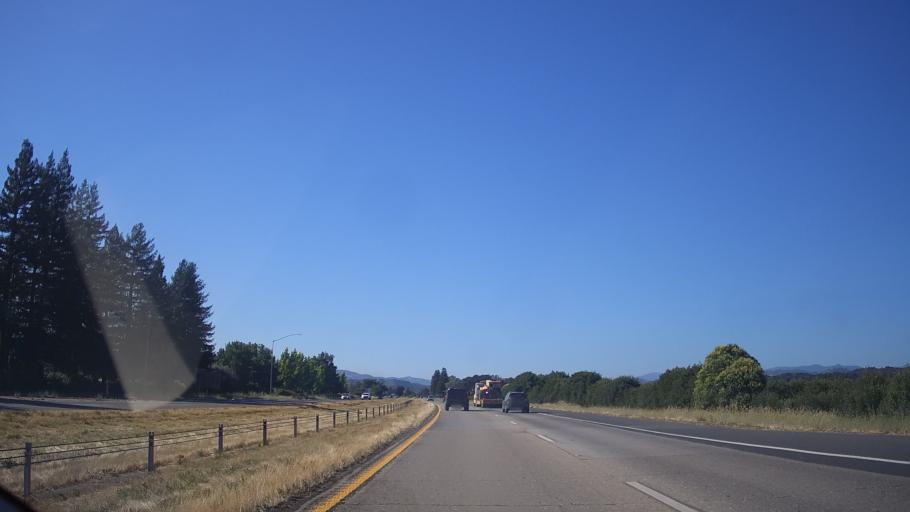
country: US
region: California
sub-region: Mendocino County
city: Ukiah
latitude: 39.1528
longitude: -123.1969
